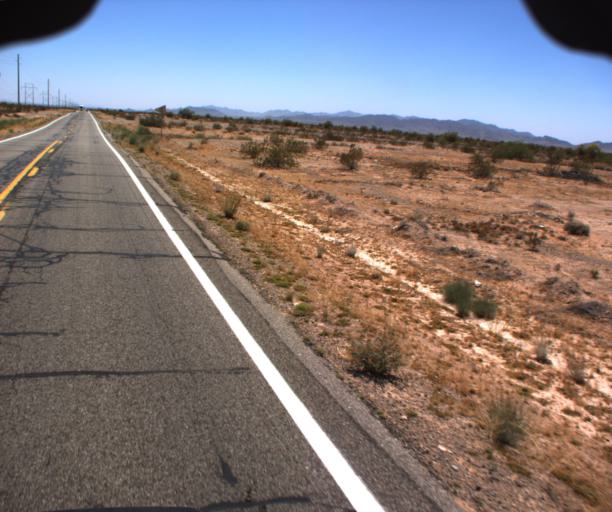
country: US
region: Arizona
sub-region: La Paz County
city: Quartzsite
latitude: 33.8233
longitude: -114.2170
